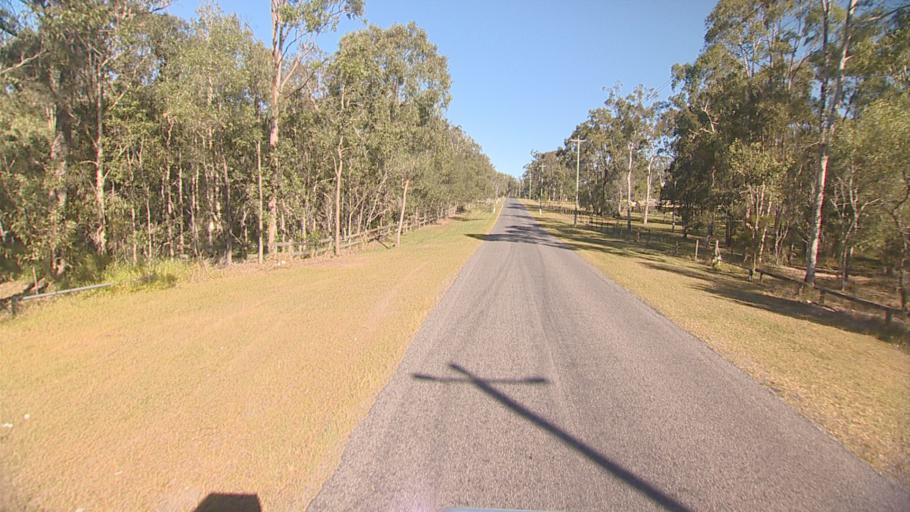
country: AU
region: Queensland
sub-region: Logan
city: Chambers Flat
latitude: -27.7360
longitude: 153.0711
